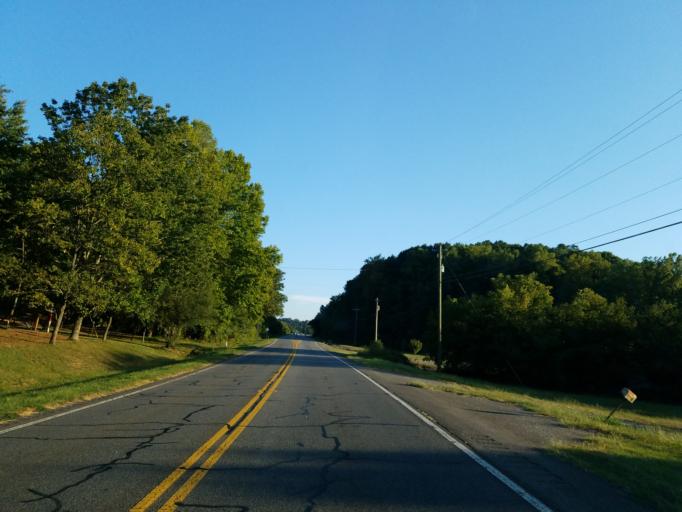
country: US
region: Georgia
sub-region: Bartow County
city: Rydal
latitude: 34.3978
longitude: -84.7089
